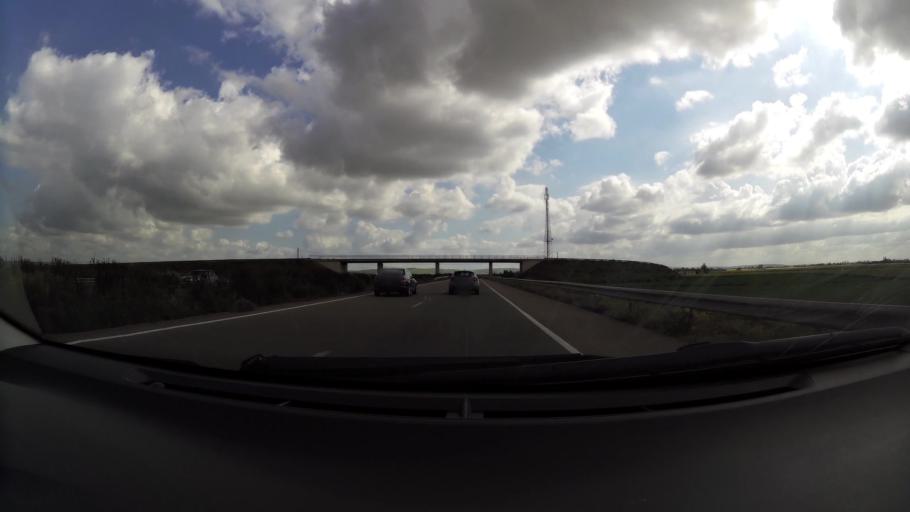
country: MA
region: Chaouia-Ouardigha
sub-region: Settat Province
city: Berrechid
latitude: 33.1367
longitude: -7.5768
